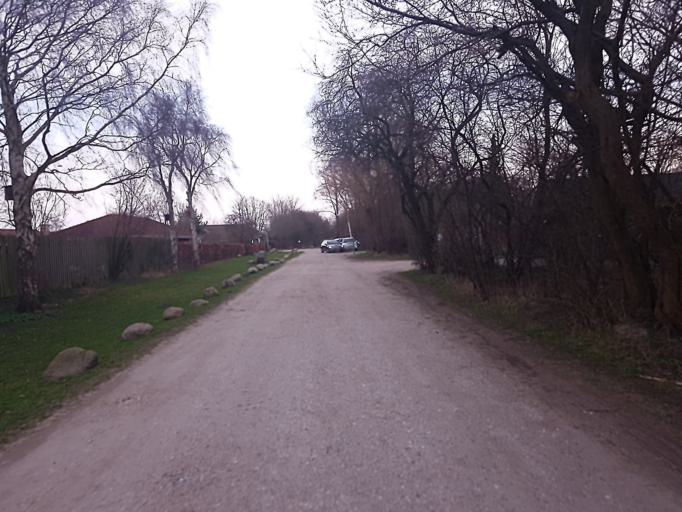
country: DK
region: Capital Region
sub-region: Tarnby Kommune
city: Tarnby
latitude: 55.6014
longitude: 12.5758
